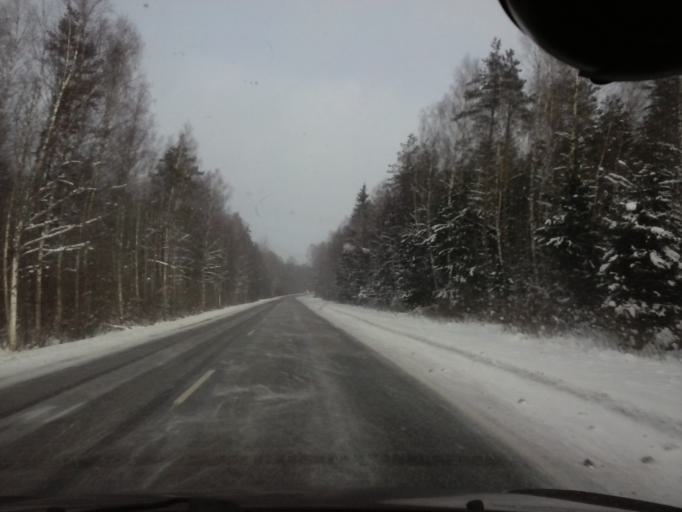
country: EE
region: Viljandimaa
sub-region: Suure-Jaani vald
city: Suure-Jaani
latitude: 58.3480
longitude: 25.3646
